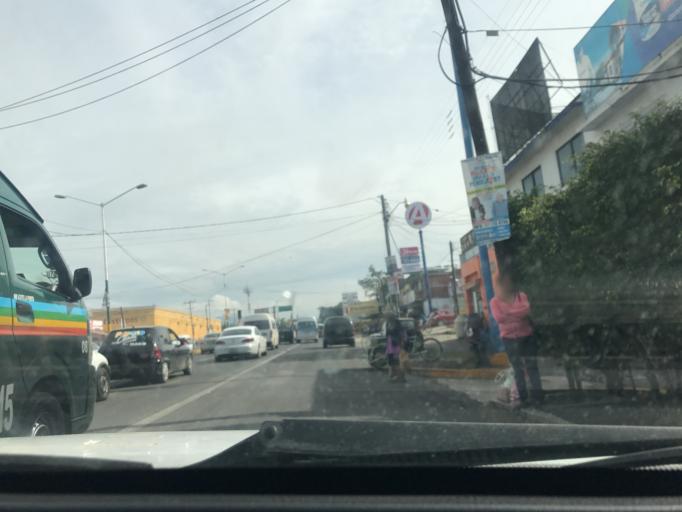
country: MX
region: Morelos
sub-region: Cuautla
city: Tierra Larga (Campo Nuevo)
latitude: 18.8660
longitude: -98.9296
